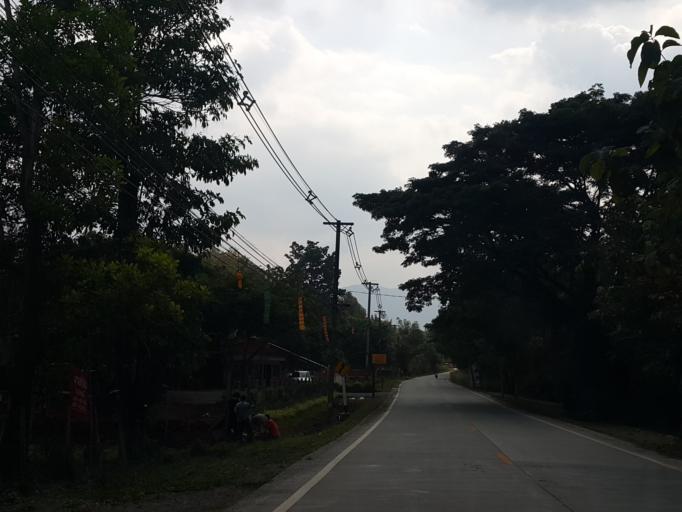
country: TH
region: Chiang Mai
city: Mae On
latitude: 18.8036
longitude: 99.2384
